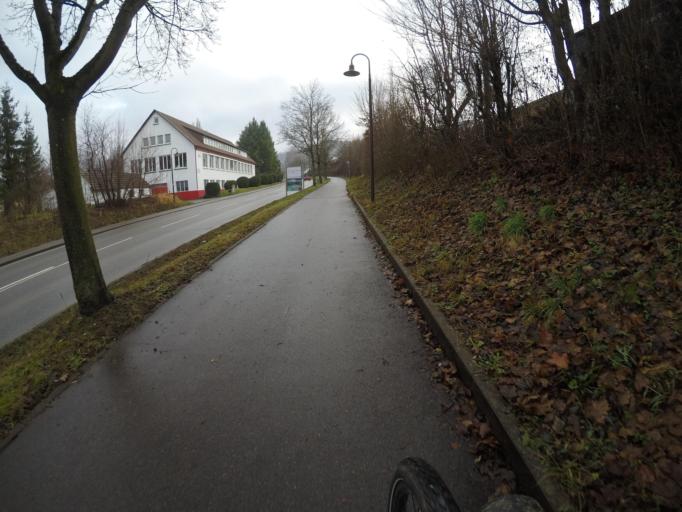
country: DE
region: Baden-Wuerttemberg
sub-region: Regierungsbezirk Stuttgart
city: Beuren
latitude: 48.5738
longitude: 9.3936
